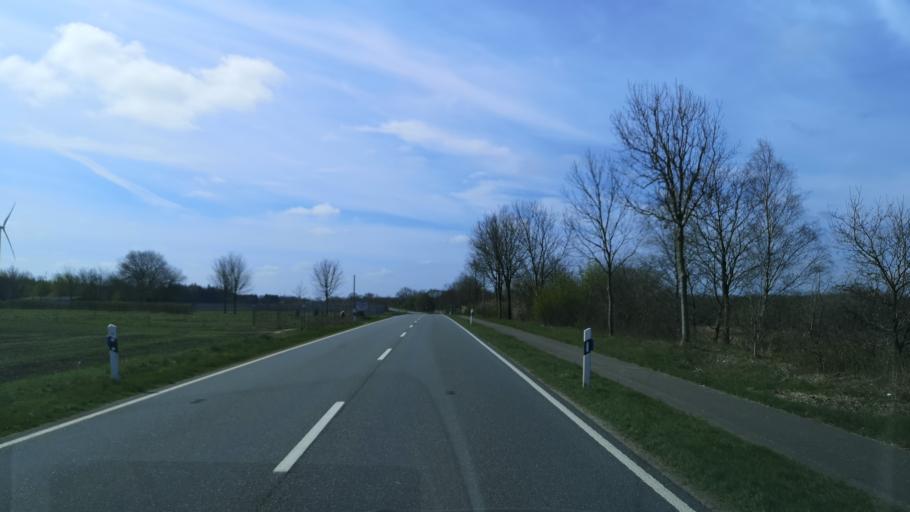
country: DE
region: Schleswig-Holstein
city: Albersdorf
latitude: 54.1250
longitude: 9.2743
